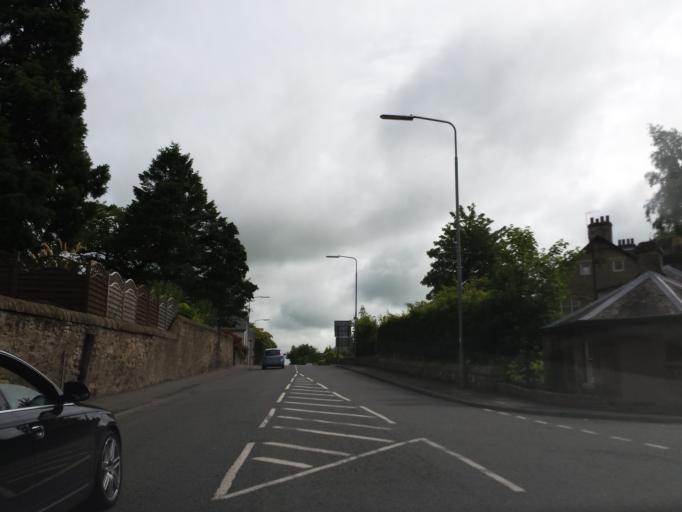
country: GB
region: Scotland
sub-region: Fife
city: Cupar
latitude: 56.3206
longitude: -3.0069
